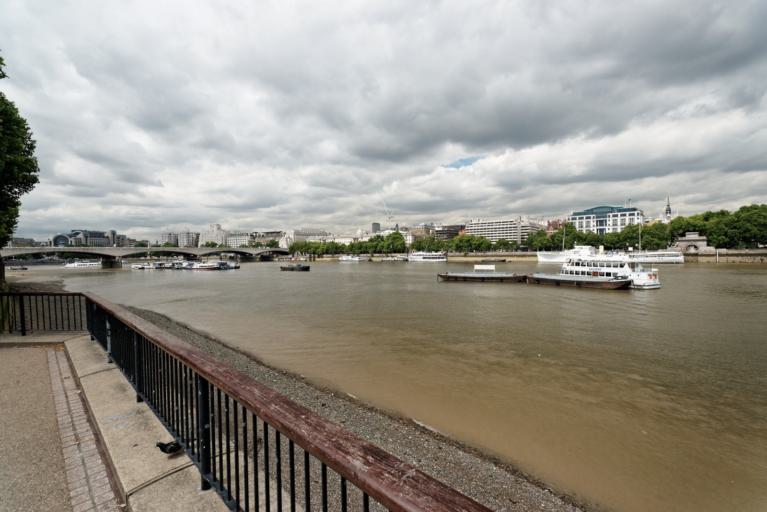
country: GB
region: England
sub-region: Greater London
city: City of Westminster
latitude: 51.5085
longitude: -0.1110
